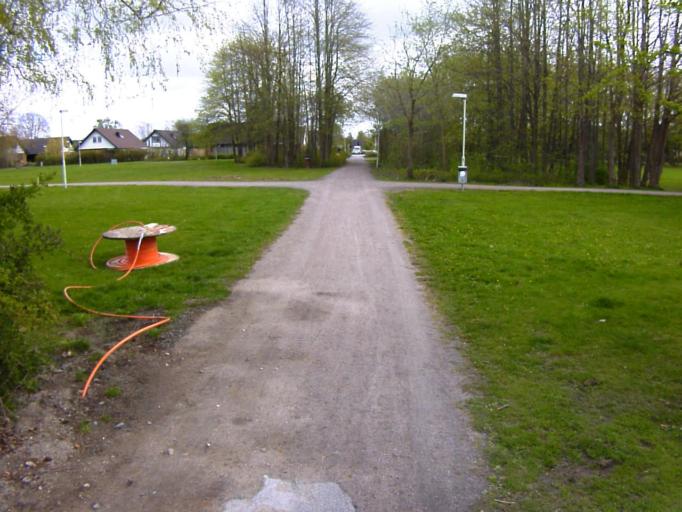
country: SE
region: Skane
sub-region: Kristianstads Kommun
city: Kristianstad
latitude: 56.0466
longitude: 14.1837
